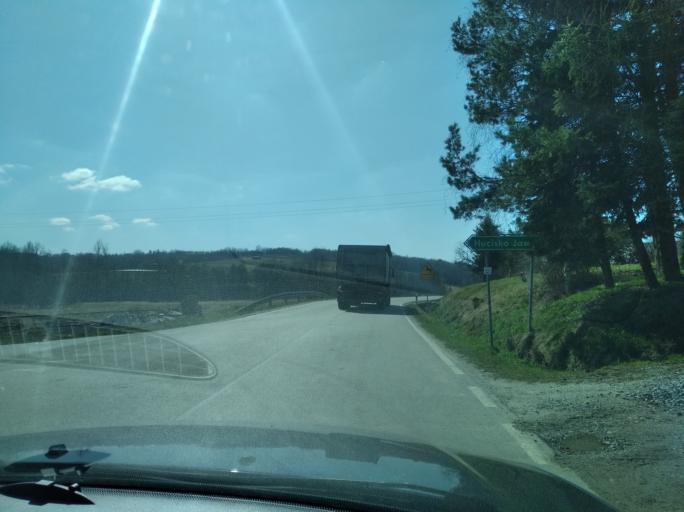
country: PL
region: Subcarpathian Voivodeship
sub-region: Powiat przeworski
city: Jawornik Polski
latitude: 49.9032
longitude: 22.3070
